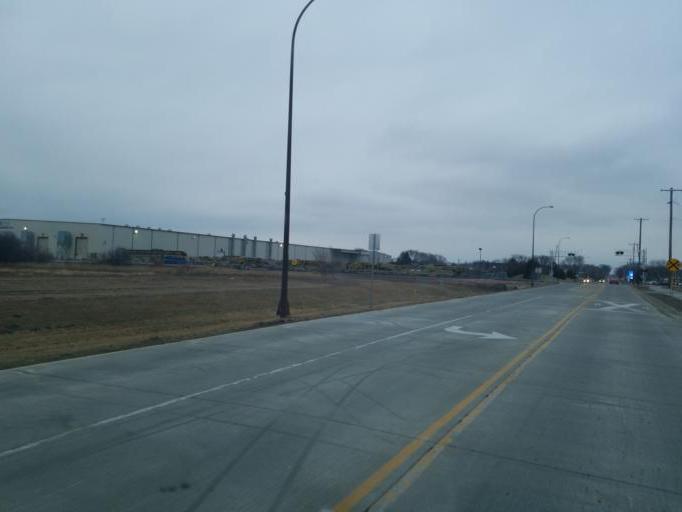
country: US
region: South Dakota
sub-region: Yankton County
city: Yankton
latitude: 42.8907
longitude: -97.4065
